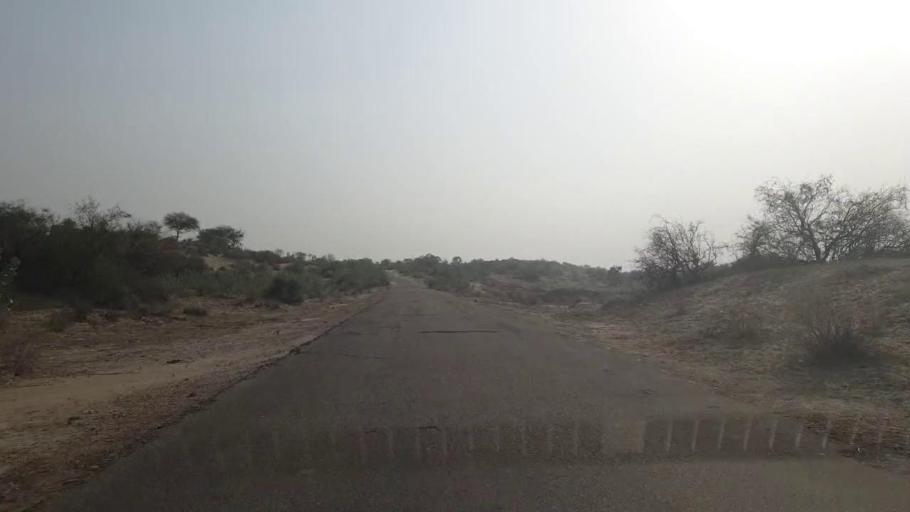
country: PK
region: Sindh
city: Chor
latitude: 25.4711
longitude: 69.9699
